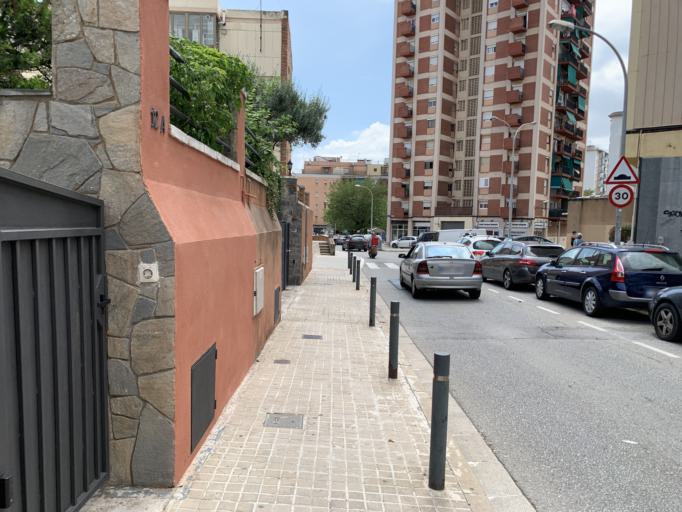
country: ES
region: Catalonia
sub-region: Provincia de Barcelona
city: Cerdanyola del Valles
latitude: 41.4945
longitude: 2.1345
